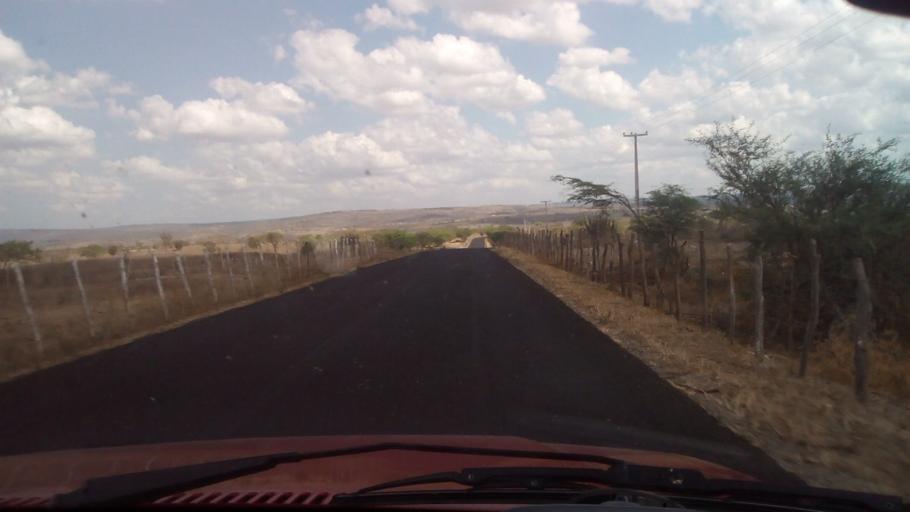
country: BR
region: Paraiba
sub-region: Cacimba De Dentro
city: Cacimba de Dentro
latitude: -6.6673
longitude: -35.7571
